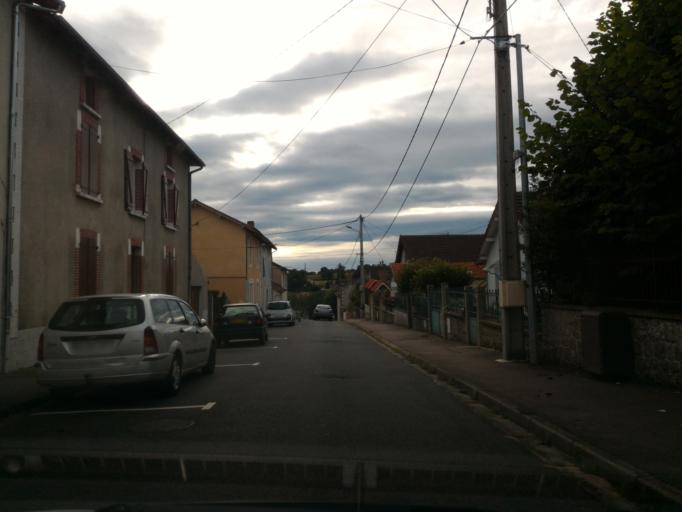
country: FR
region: Limousin
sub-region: Departement de la Haute-Vienne
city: Saint-Junien
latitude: 45.8882
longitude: 0.8914
